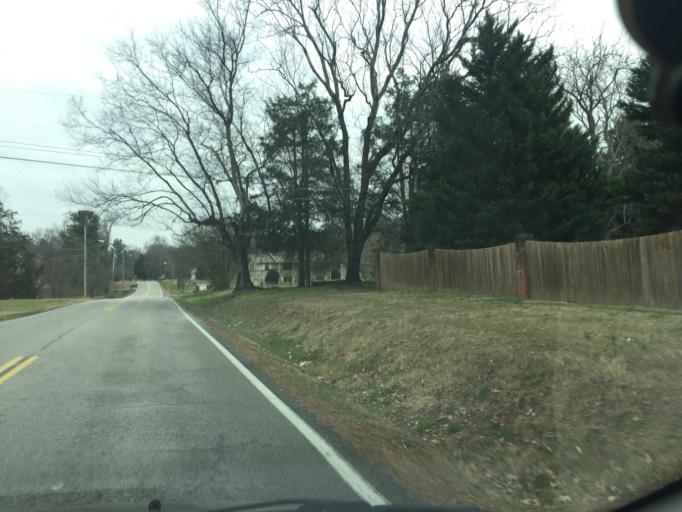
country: US
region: Tennessee
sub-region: Hamilton County
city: East Brainerd
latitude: 35.0082
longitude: -85.1288
